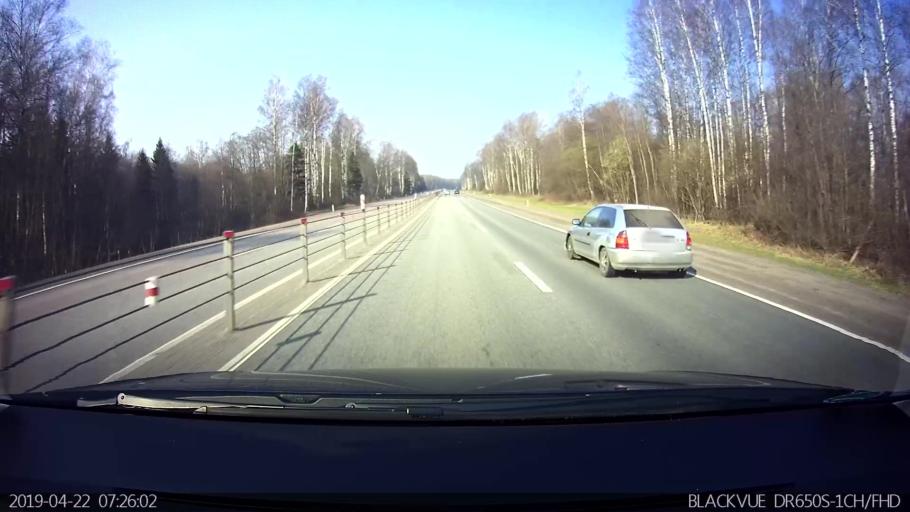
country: RU
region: Smolensk
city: Vyaz'ma
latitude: 55.1897
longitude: 34.0723
